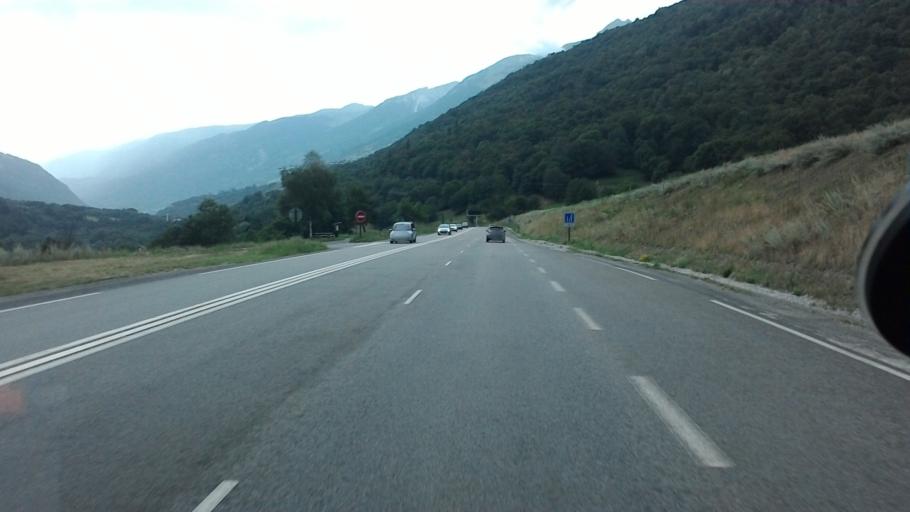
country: FR
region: Rhone-Alpes
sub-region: Departement de la Savoie
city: Macot-la-Plagne
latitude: 45.5680
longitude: 6.7091
